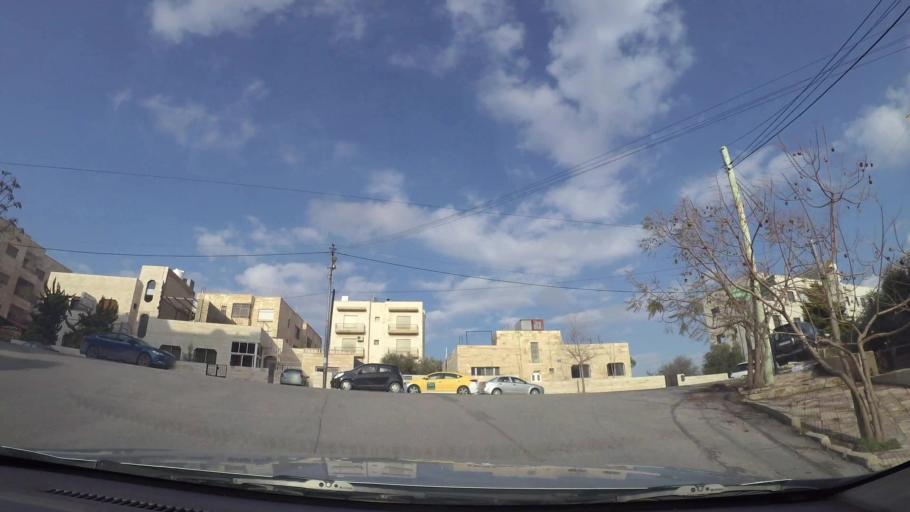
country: JO
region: Amman
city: Al Jubayhah
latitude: 31.9871
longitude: 35.8560
